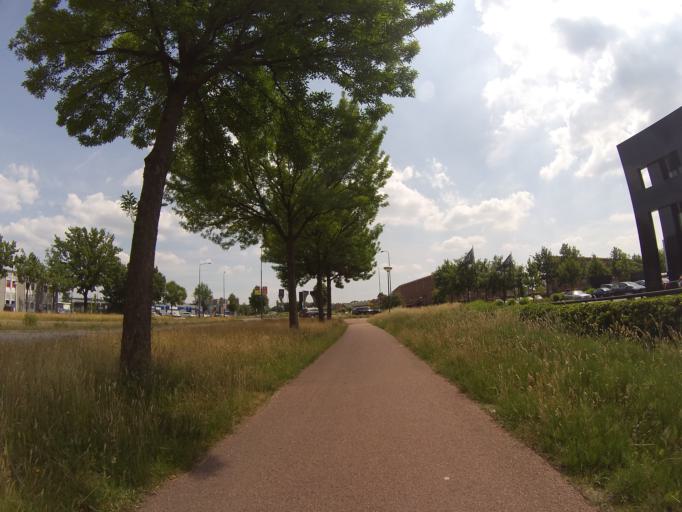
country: NL
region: Utrecht
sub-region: Gemeente Soest
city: Soest
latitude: 52.1771
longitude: 5.2721
